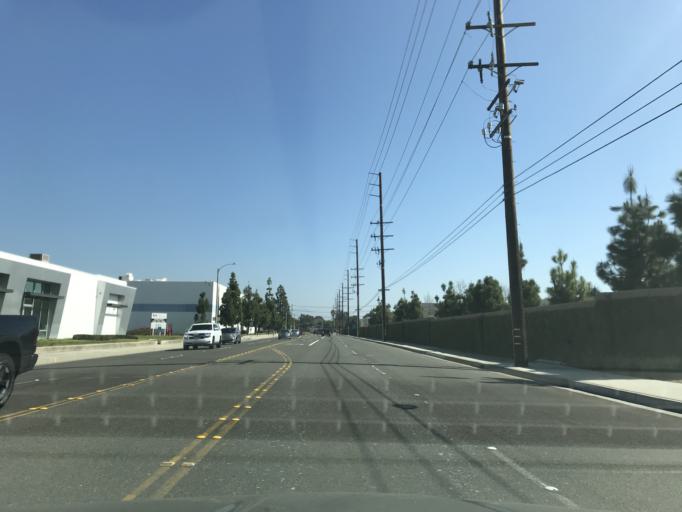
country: US
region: California
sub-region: Orange County
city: Fountain Valley
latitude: 33.6944
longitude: -117.9414
